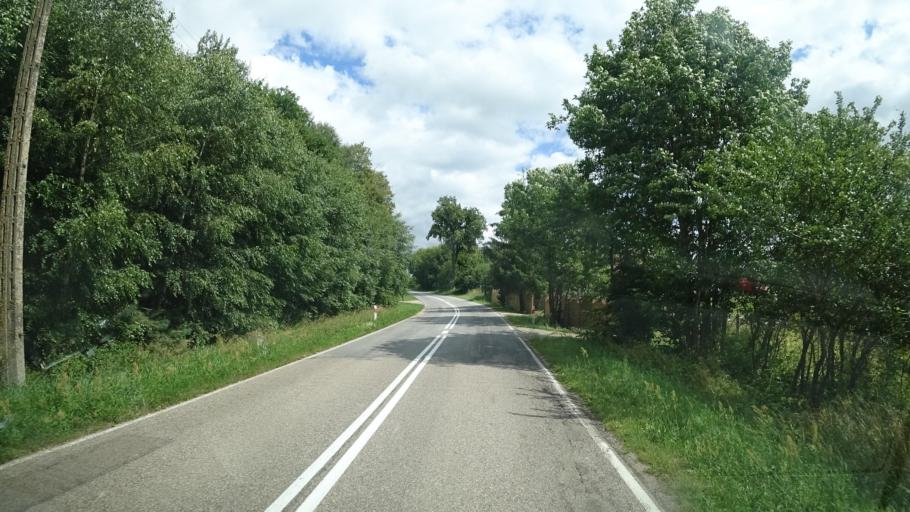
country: PL
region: Warmian-Masurian Voivodeship
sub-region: Powiat goldapski
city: Goldap
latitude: 54.2082
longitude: 22.1936
